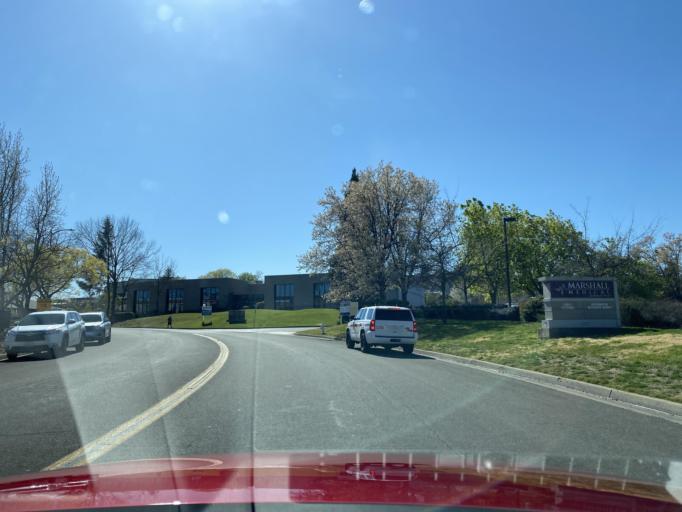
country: US
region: California
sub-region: El Dorado County
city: El Dorado Hills
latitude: 38.6399
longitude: -121.0688
